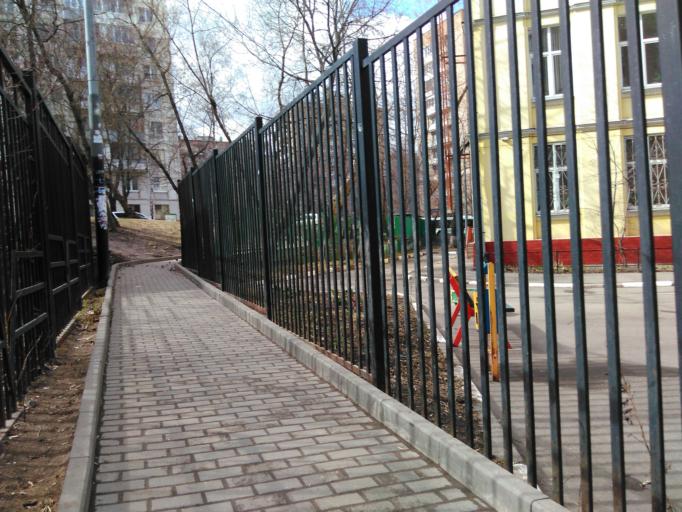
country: RU
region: Moscow
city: Mar'ina Roshcha
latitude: 55.8065
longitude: 37.6418
